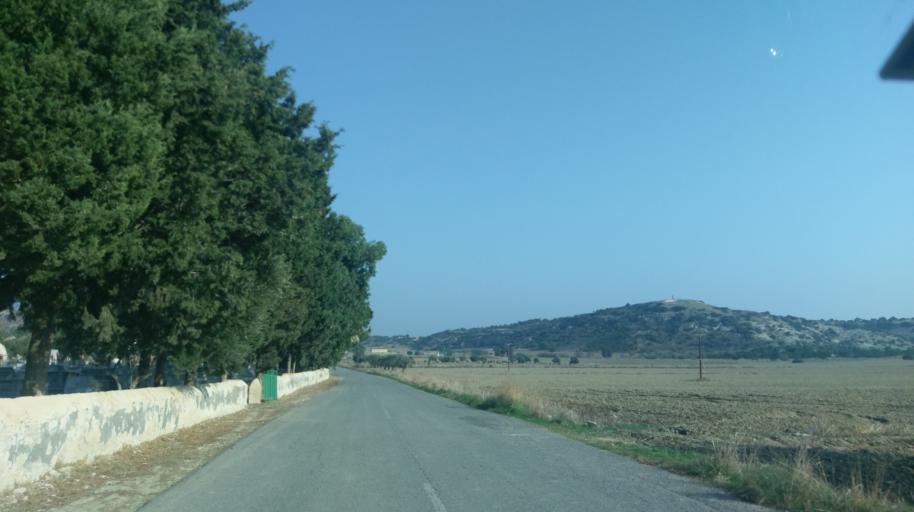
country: CY
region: Ammochostos
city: Rizokarpaso
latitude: 35.5150
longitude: 34.2971
